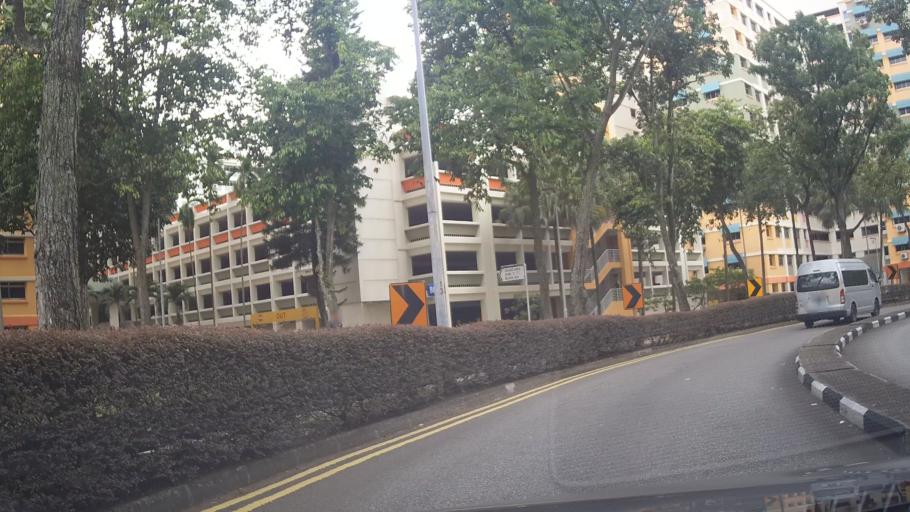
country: MY
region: Johor
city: Johor Bahru
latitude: 1.4437
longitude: 103.7915
